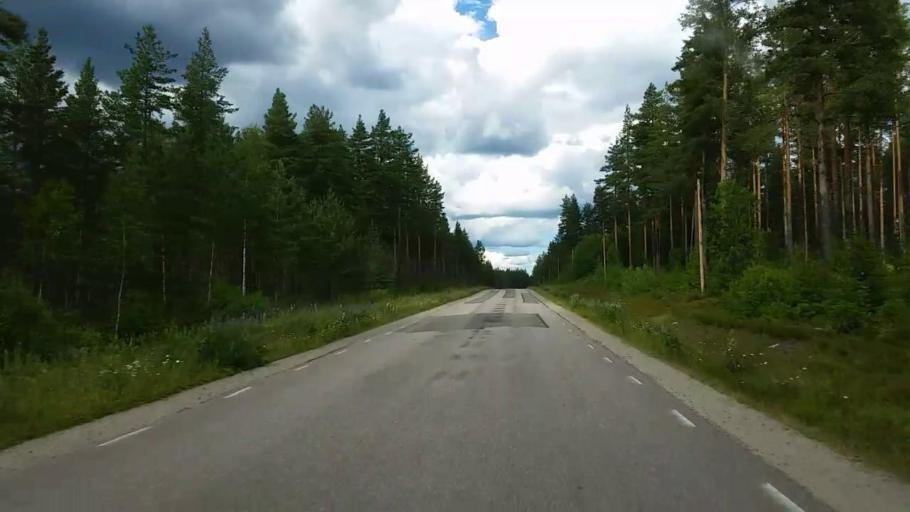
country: SE
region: Gaevleborg
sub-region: Ovanakers Kommun
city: Edsbyn
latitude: 61.4050
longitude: 15.8965
